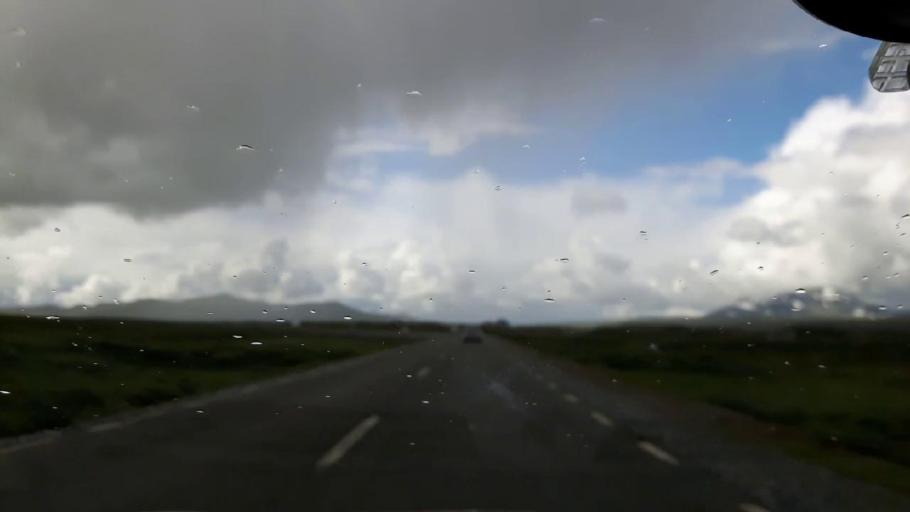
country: NO
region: Nordland
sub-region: Hattfjelldal
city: Hattfjelldal
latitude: 65.1043
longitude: 14.4720
